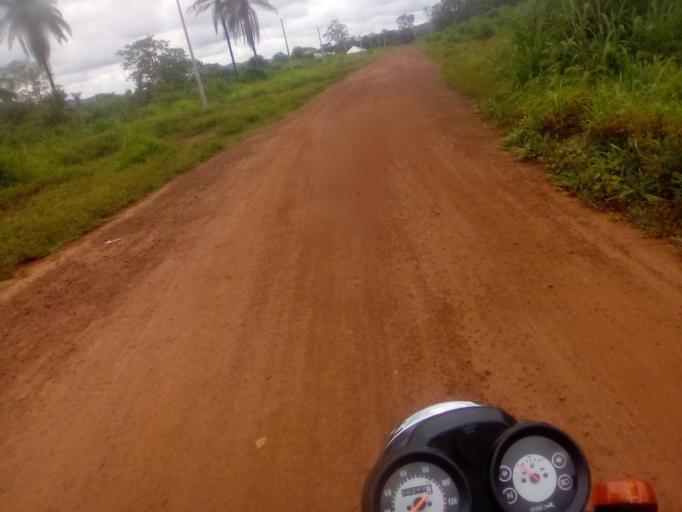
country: SL
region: Southern Province
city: Moyamba
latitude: 8.1438
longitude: -12.4397
